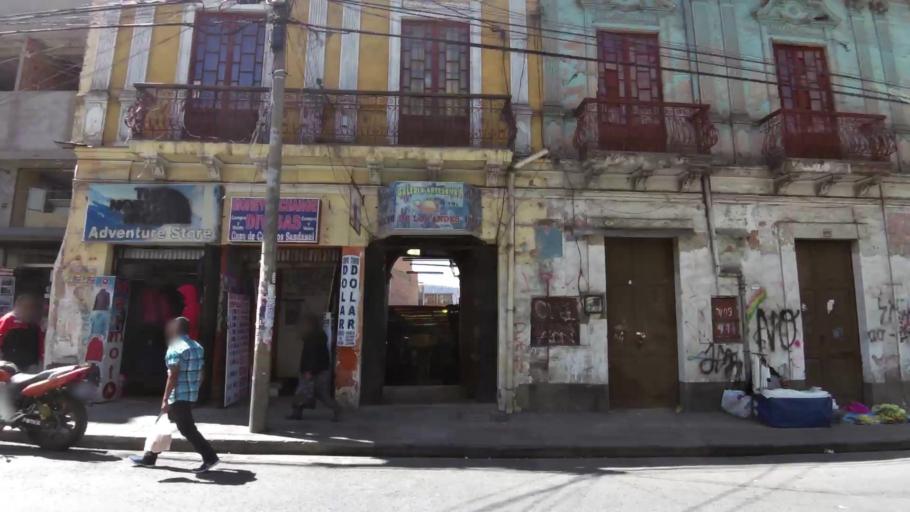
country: BO
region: La Paz
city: La Paz
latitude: -16.4971
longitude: -68.1396
